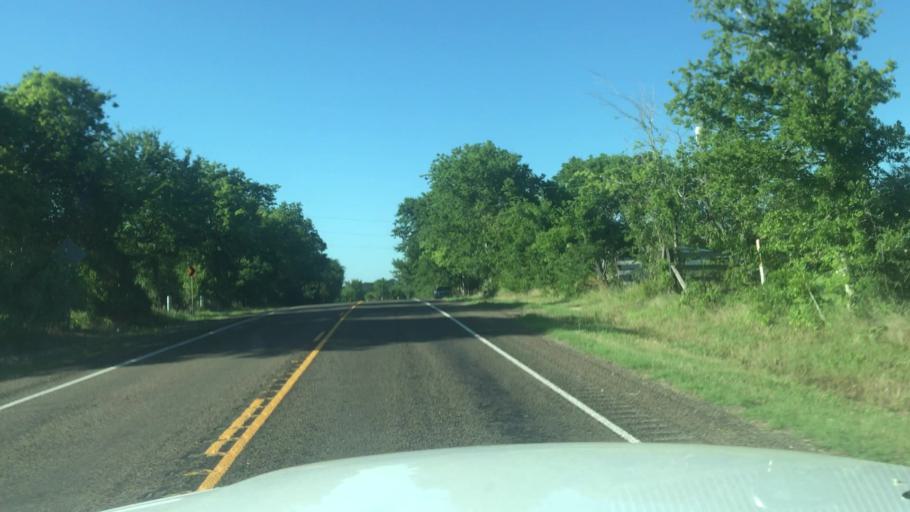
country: US
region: Texas
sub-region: Grimes County
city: Anderson
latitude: 30.6244
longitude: -95.8831
